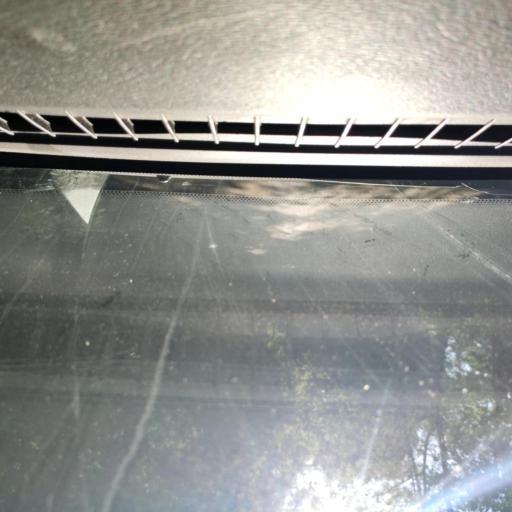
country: RU
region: Perm
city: Overyata
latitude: 58.1242
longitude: 55.8717
